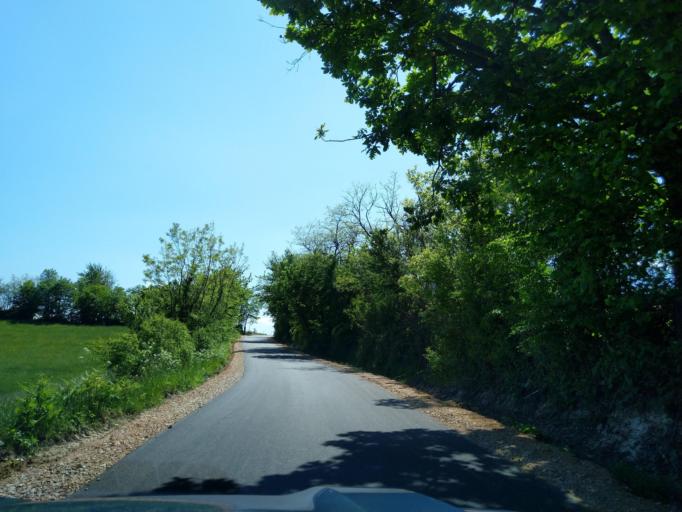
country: RS
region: Central Serbia
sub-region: Zlatiborski Okrug
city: Uzice
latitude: 43.8572
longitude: 19.9159
